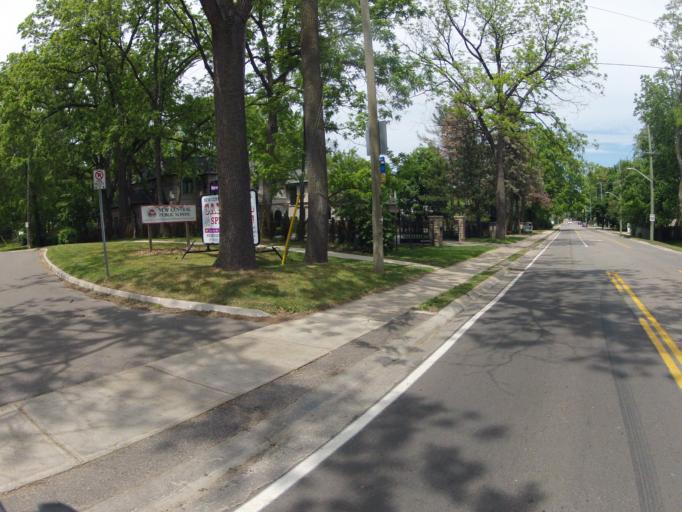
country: CA
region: Ontario
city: Oakville
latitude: 43.4533
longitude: -79.6601
